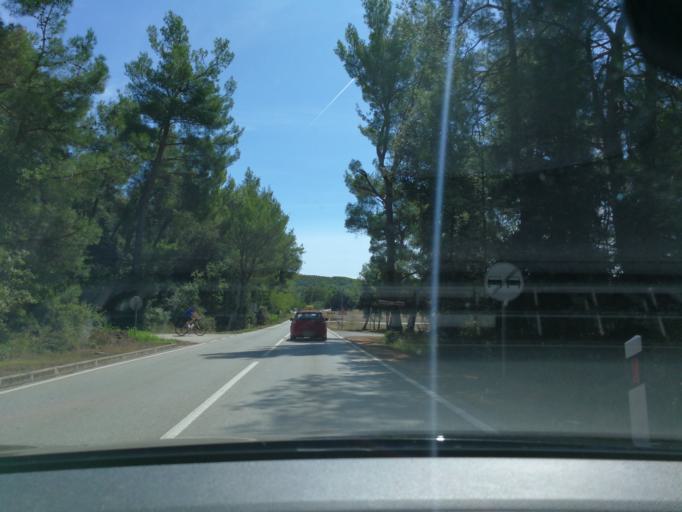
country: HR
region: Istarska
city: Medulin
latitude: 44.8226
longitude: 13.8797
